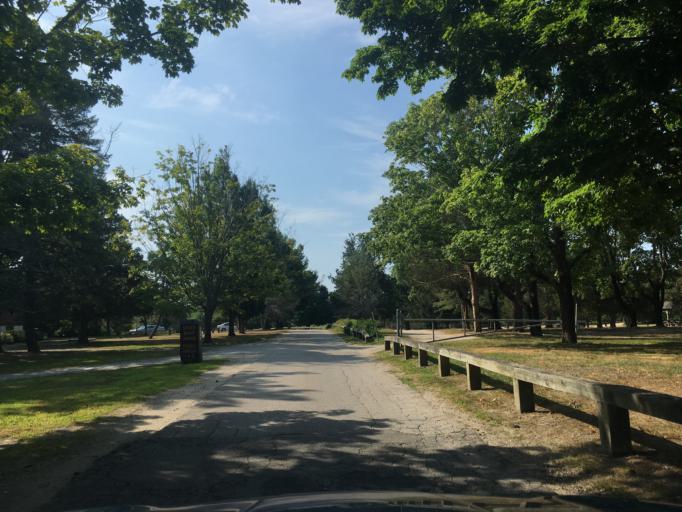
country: US
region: Rhode Island
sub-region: Kent County
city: East Greenwich
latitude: 41.6608
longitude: -71.4317
